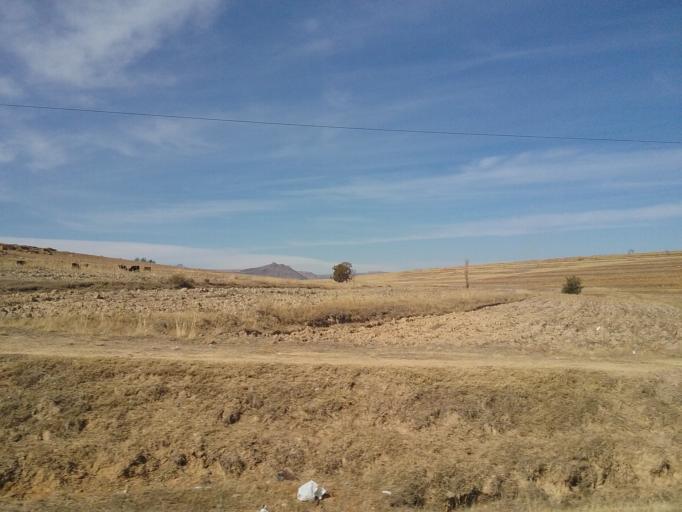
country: LS
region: Maseru
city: Maseru
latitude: -29.4597
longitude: 27.5426
